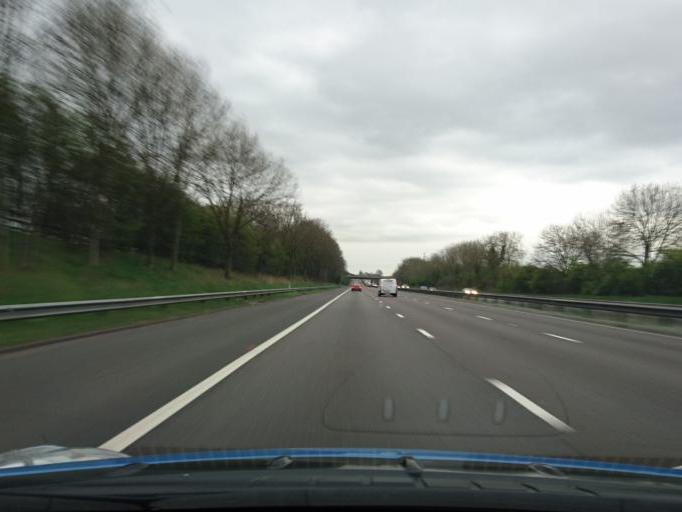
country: GB
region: England
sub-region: Staffordshire
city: Stone
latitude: 52.8550
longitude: -2.1613
